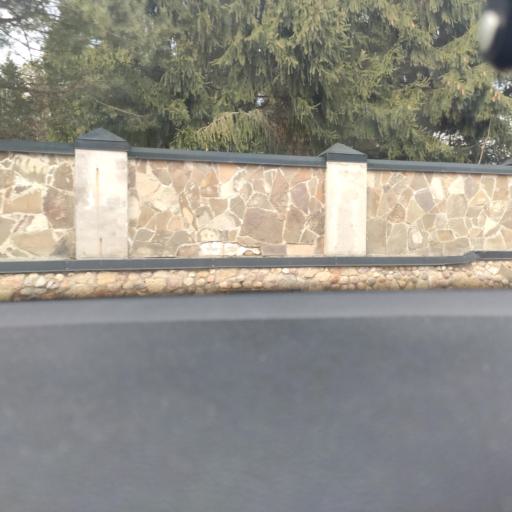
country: RU
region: Moskovskaya
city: Gorki Vtoryye
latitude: 55.7104
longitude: 37.1585
